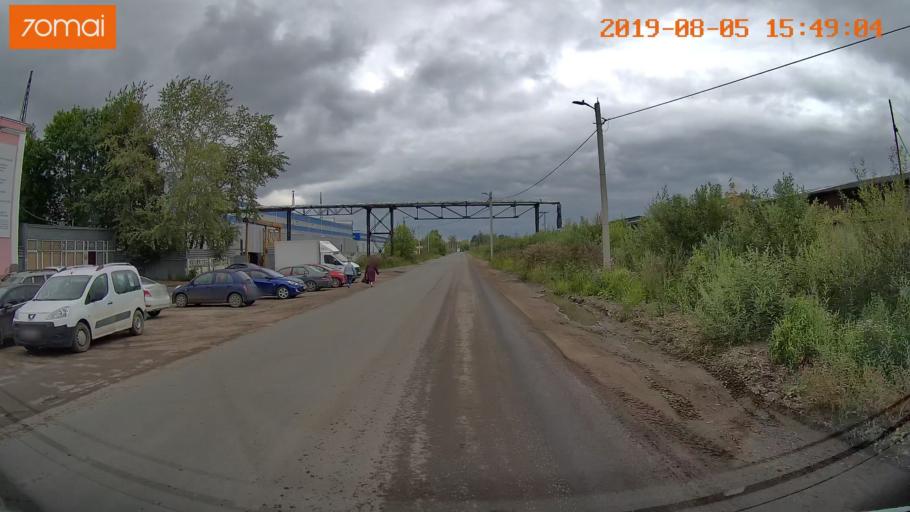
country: RU
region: Ivanovo
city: Novo-Talitsy
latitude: 56.9911
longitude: 40.9090
